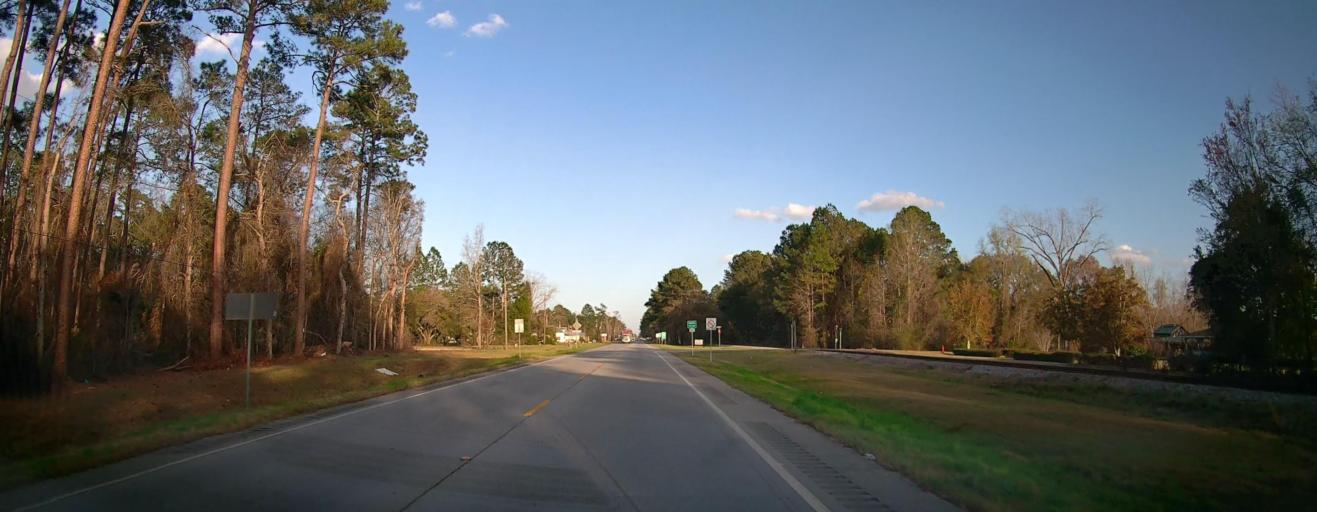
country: US
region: Georgia
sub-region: Bryan County
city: Pembroke
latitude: 32.1370
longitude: -81.6423
